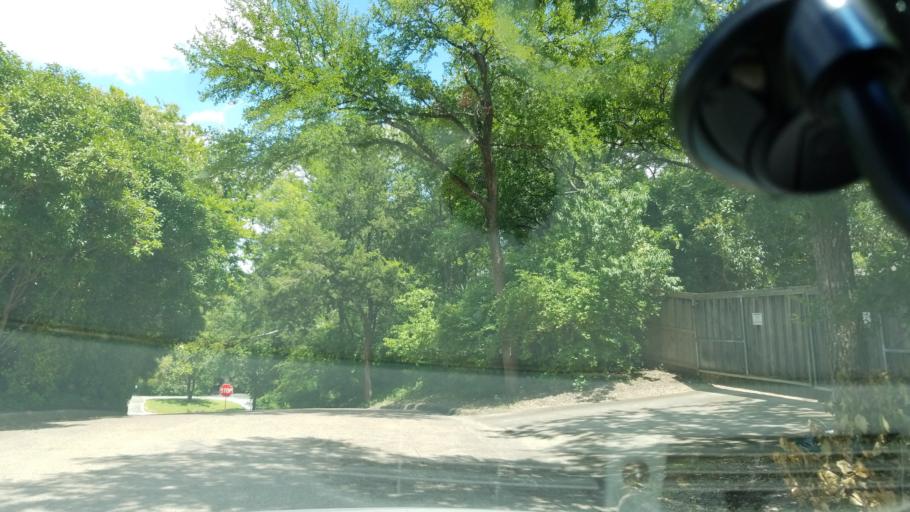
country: US
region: Texas
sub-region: Dallas County
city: Cockrell Hill
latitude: 32.6961
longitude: -96.8590
